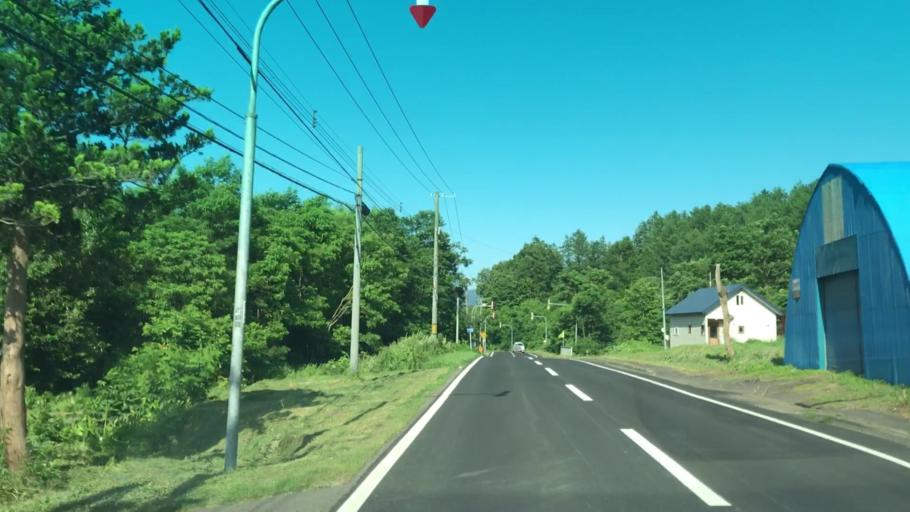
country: JP
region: Hokkaido
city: Yoichi
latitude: 43.0328
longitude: 140.7728
